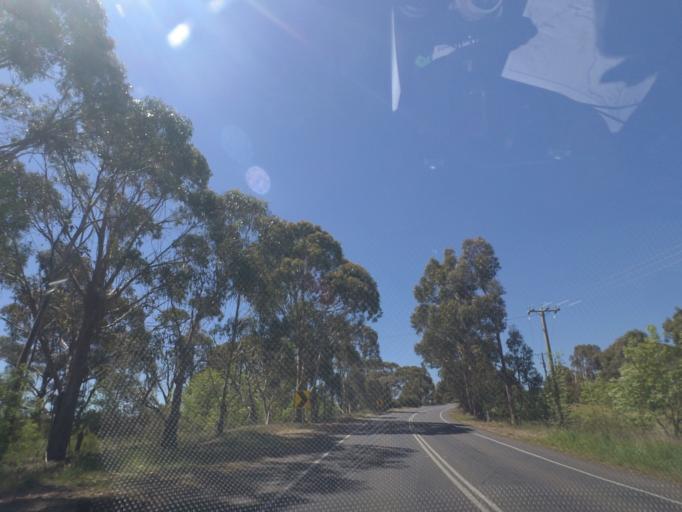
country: AU
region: Victoria
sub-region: Hume
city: Sunbury
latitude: -37.4267
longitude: 144.7196
